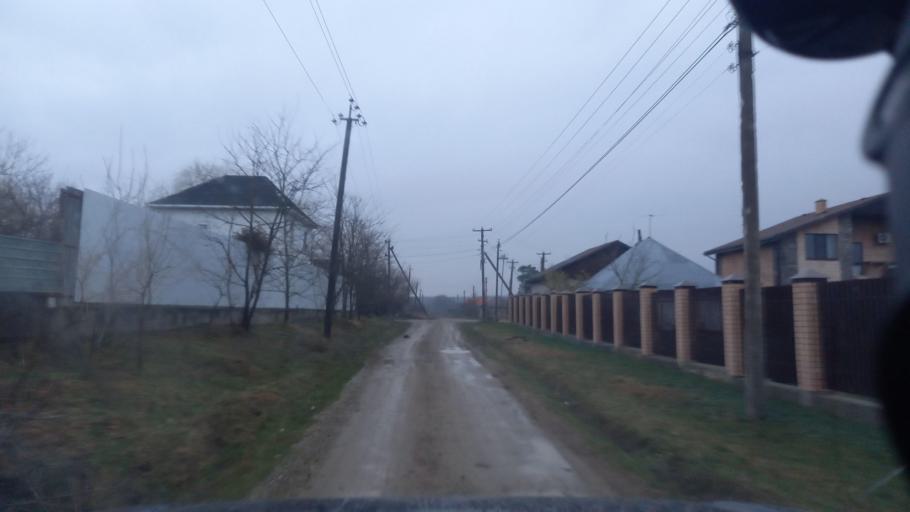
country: RU
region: Krasnodarskiy
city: Saratovskaya
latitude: 44.6470
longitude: 39.3150
